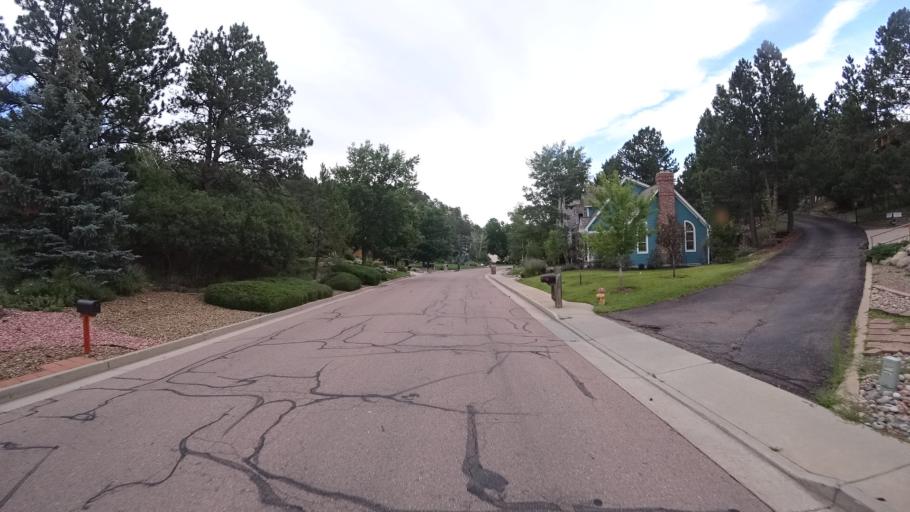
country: US
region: Colorado
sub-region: El Paso County
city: Colorado Springs
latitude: 38.9092
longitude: -104.8410
